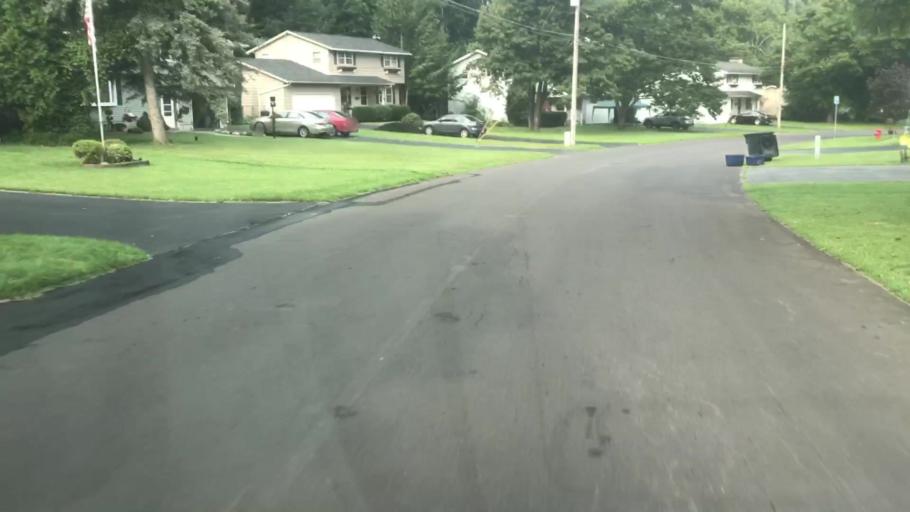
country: US
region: New York
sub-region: Onondaga County
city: Liverpool
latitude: 43.1343
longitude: -76.2197
